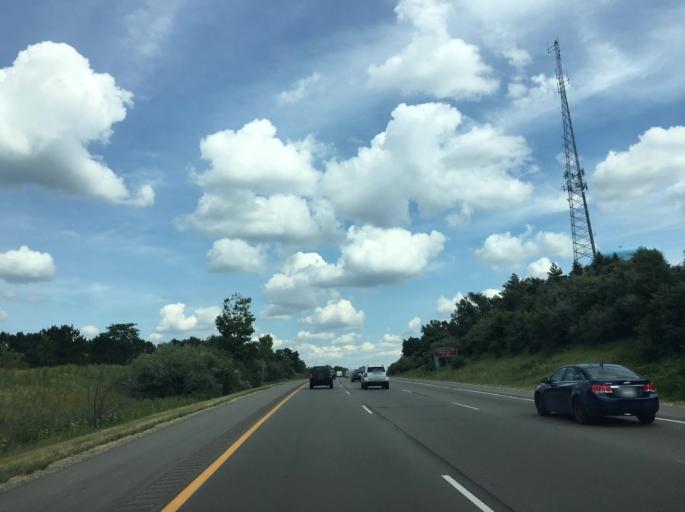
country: US
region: Michigan
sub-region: Oakland County
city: Clarkston
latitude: 42.7437
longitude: -83.3937
